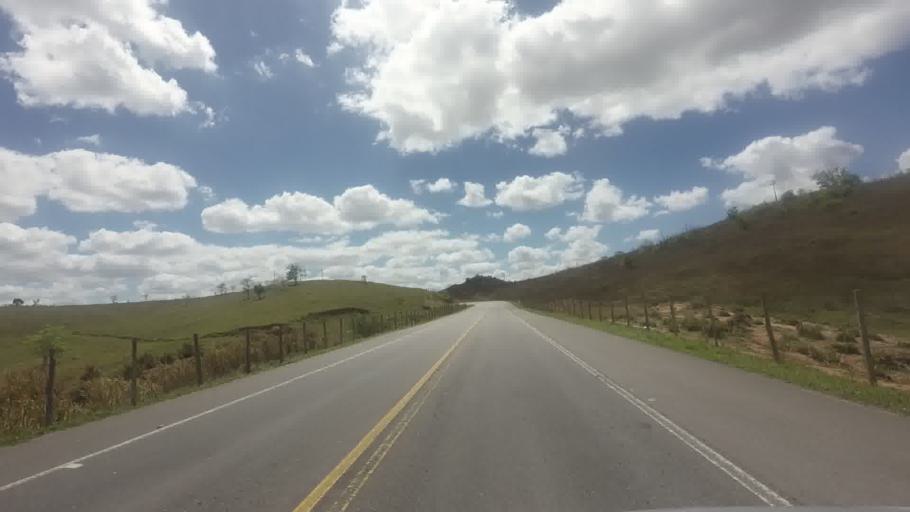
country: BR
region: Minas Gerais
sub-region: Recreio
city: Recreio
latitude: -21.6789
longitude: -42.3950
